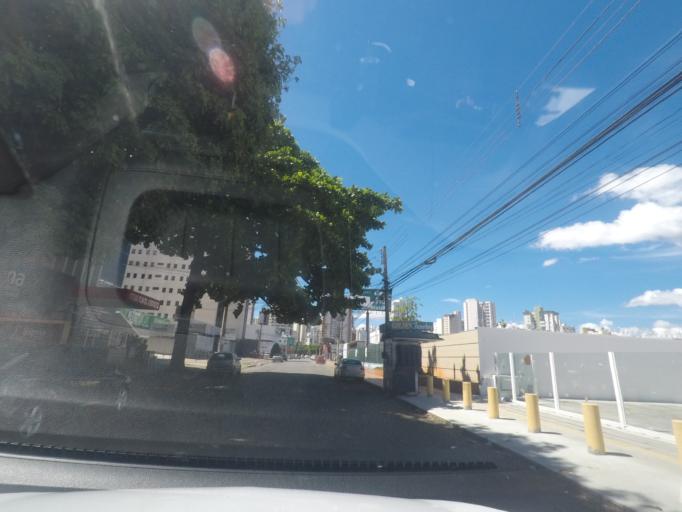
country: BR
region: Goias
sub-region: Goiania
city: Goiania
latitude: -16.6763
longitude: -49.2714
